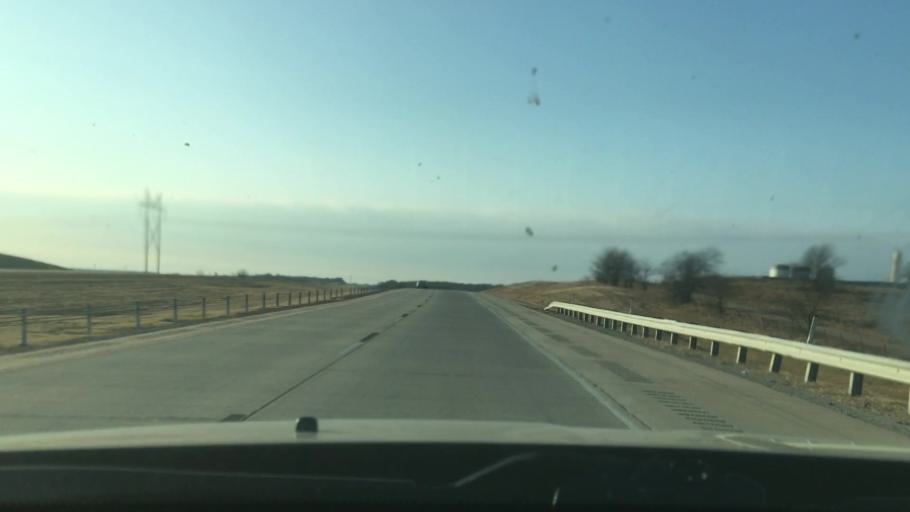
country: US
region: Oklahoma
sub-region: Carter County
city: Ardmore
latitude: 34.2548
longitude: -97.1652
